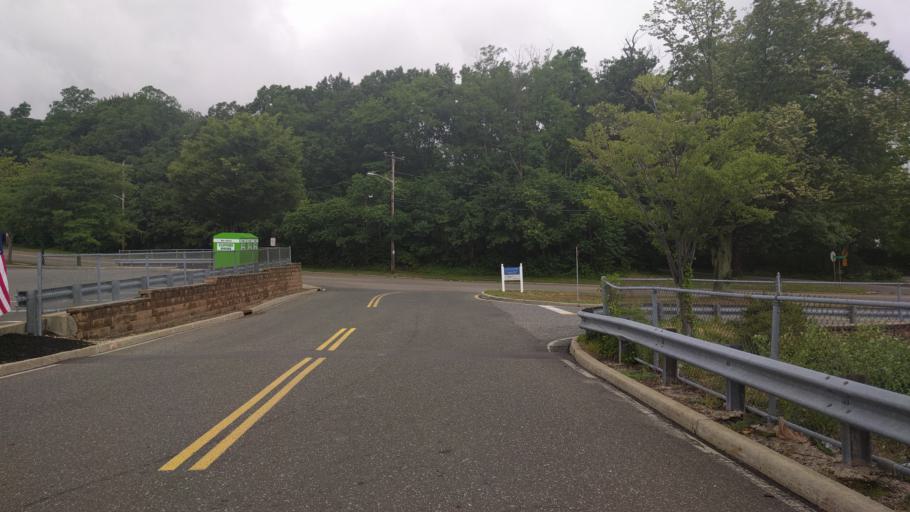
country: US
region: New York
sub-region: Suffolk County
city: Huntington Station
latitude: 40.8584
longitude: -73.4203
